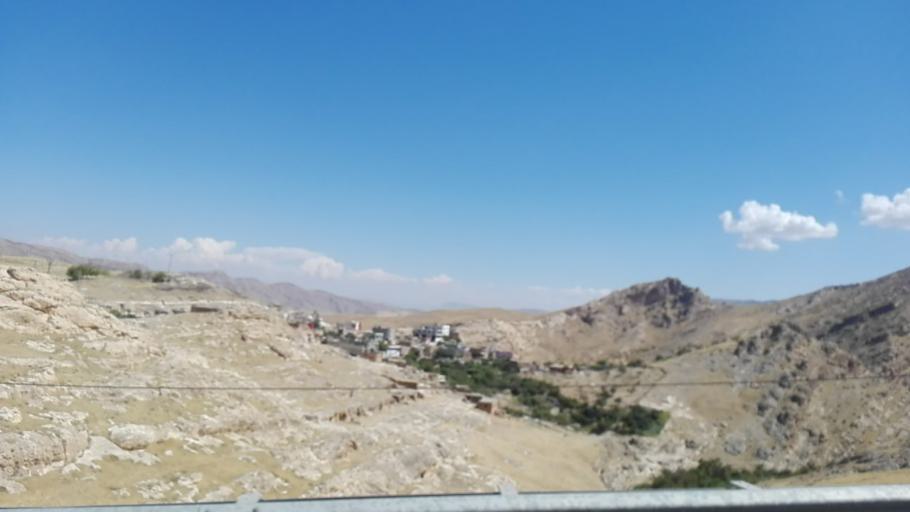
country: TR
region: Batman
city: Hasankeyf
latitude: 37.7033
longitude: 41.4621
